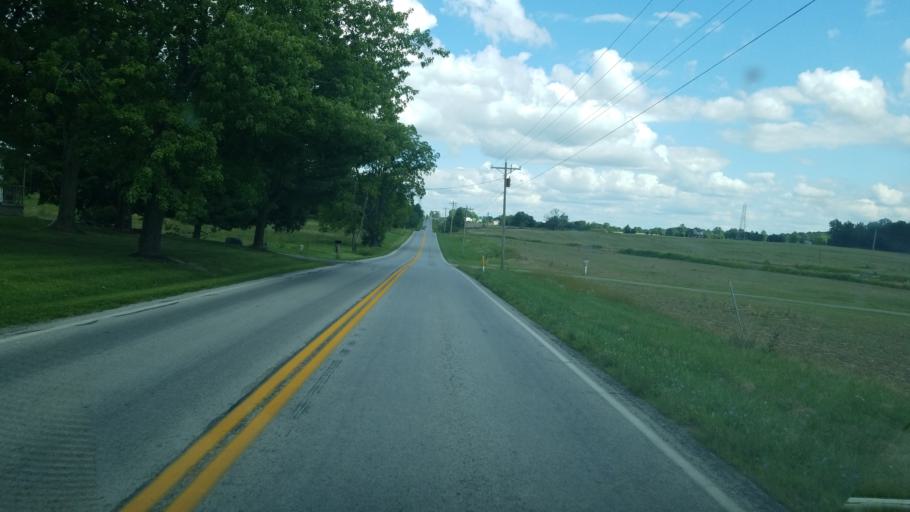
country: US
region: Ohio
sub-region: Allen County
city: Lima
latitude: 40.7888
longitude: -84.0791
